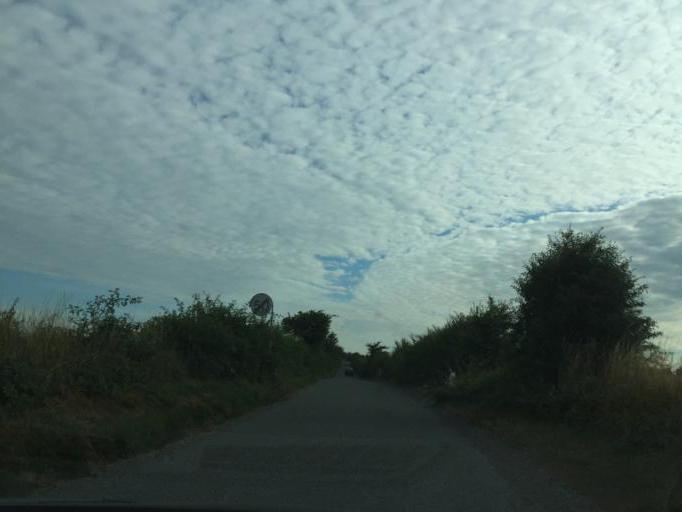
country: DK
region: South Denmark
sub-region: Assens Kommune
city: Assens
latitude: 55.2588
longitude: 9.9675
